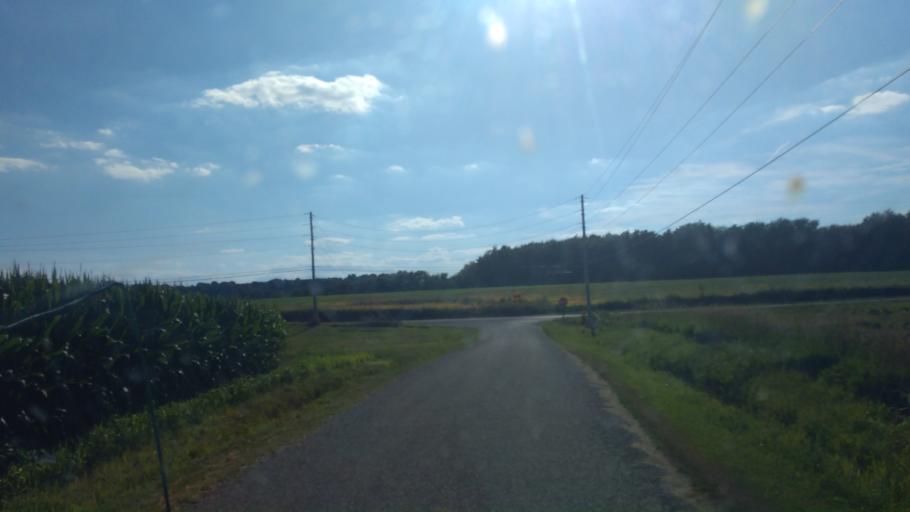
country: US
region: Ohio
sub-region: Wayne County
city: Shreve
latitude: 40.7340
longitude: -82.1065
